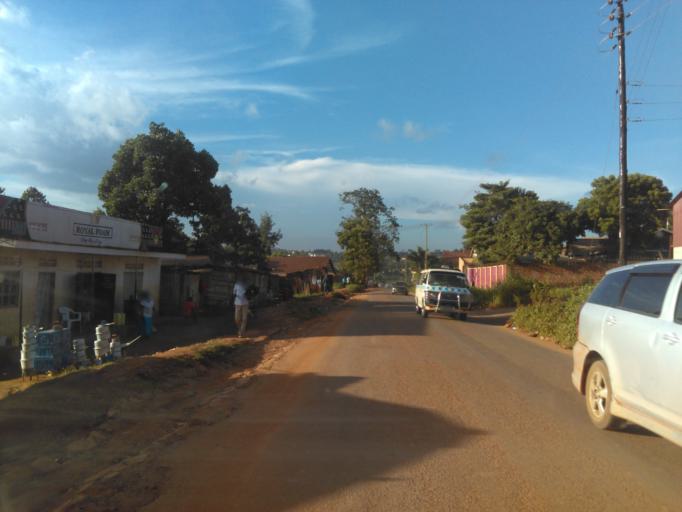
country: UG
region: Central Region
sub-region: Kampala District
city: Kampala
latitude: 0.2655
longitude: 32.5565
